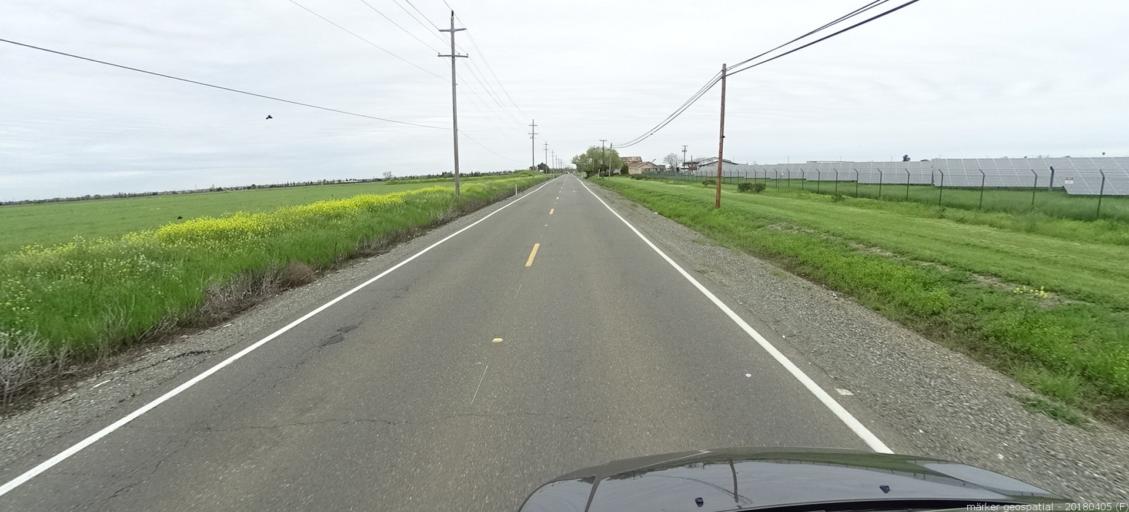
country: US
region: California
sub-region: Sacramento County
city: Laguna
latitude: 38.3659
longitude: -121.4176
